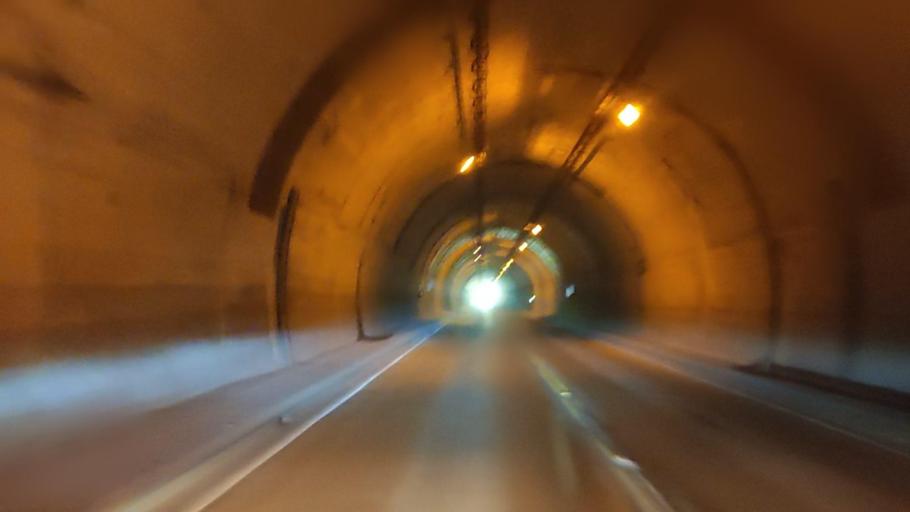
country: JP
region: Shizuoka
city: Ito
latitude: 34.9270
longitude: 139.0447
